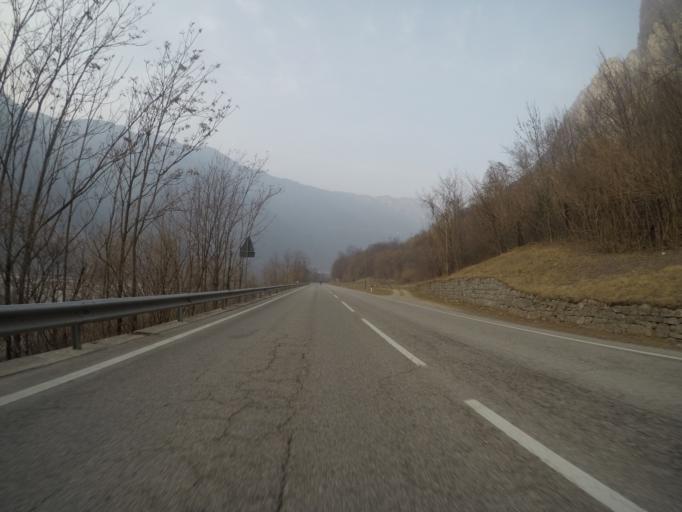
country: IT
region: Veneto
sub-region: Provincia di Belluno
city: Vas
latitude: 45.9641
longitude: 11.9376
